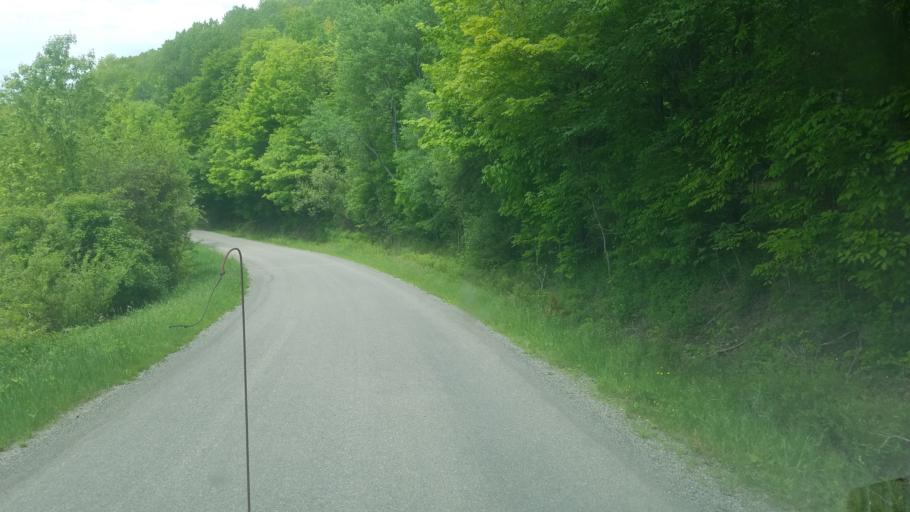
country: US
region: Pennsylvania
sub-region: Tioga County
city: Westfield
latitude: 41.8924
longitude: -77.6008
